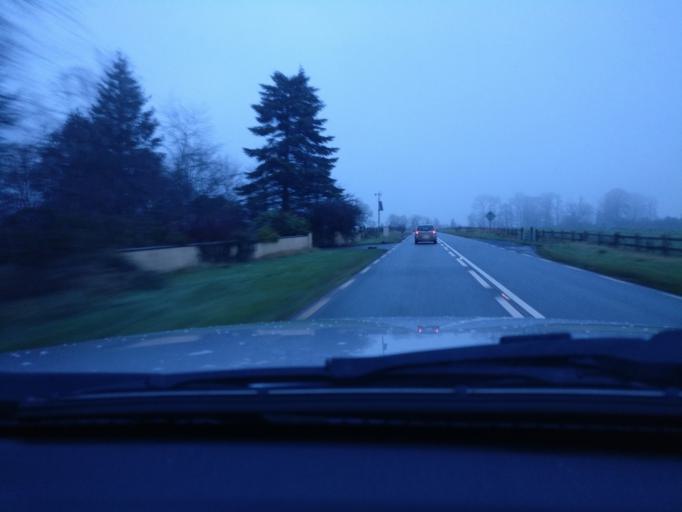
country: IE
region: Leinster
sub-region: An Mhi
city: Athboy
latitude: 53.6439
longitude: -6.8763
